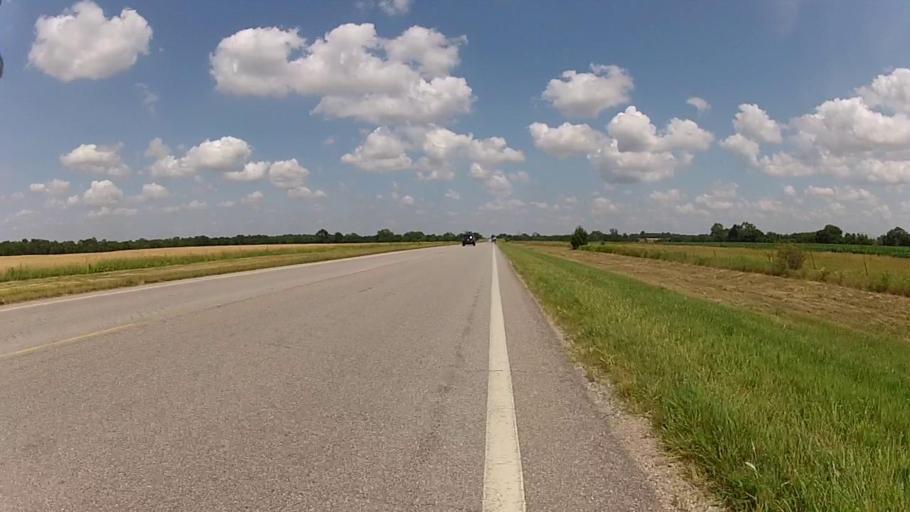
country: US
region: Kansas
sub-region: Labette County
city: Altamont
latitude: 37.1930
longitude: -95.2305
